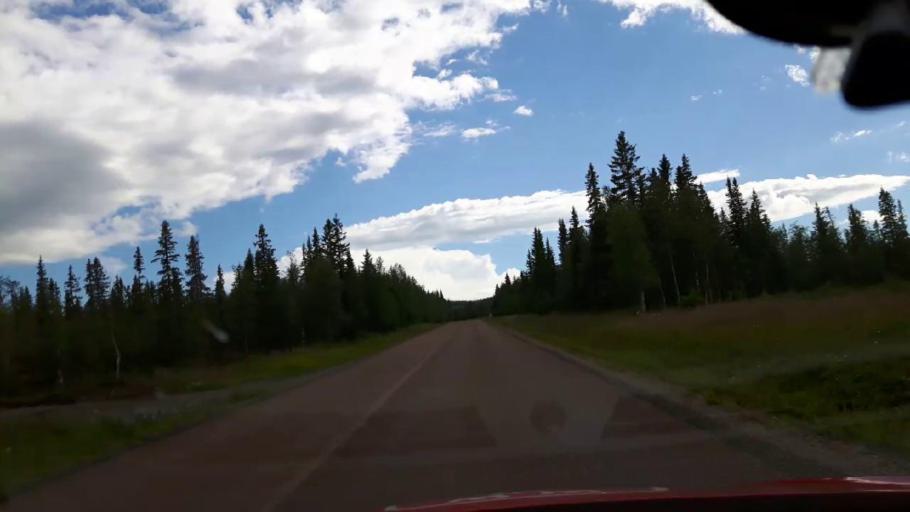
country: SE
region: Jaemtland
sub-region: Are Kommun
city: Are
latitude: 63.2934
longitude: 13.2319
